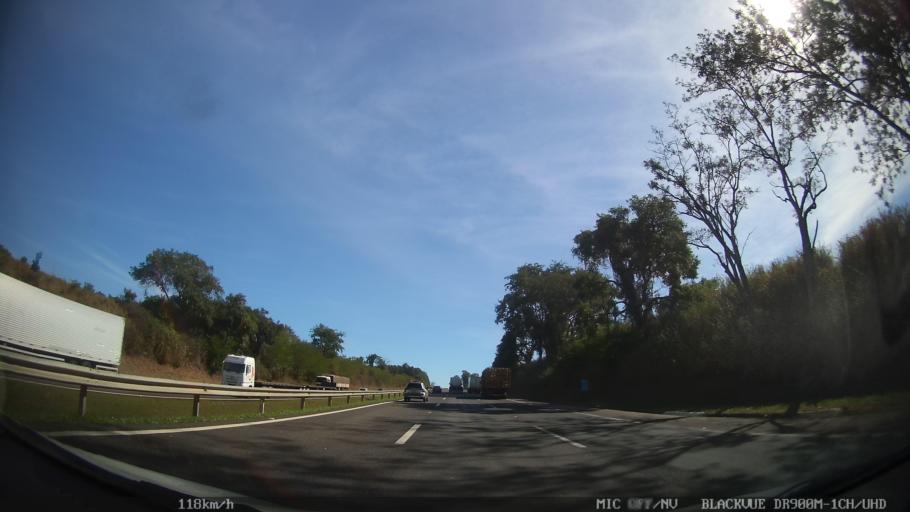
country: BR
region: Sao Paulo
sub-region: Porto Ferreira
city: Porto Ferreira
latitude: -21.7849
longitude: -47.5268
